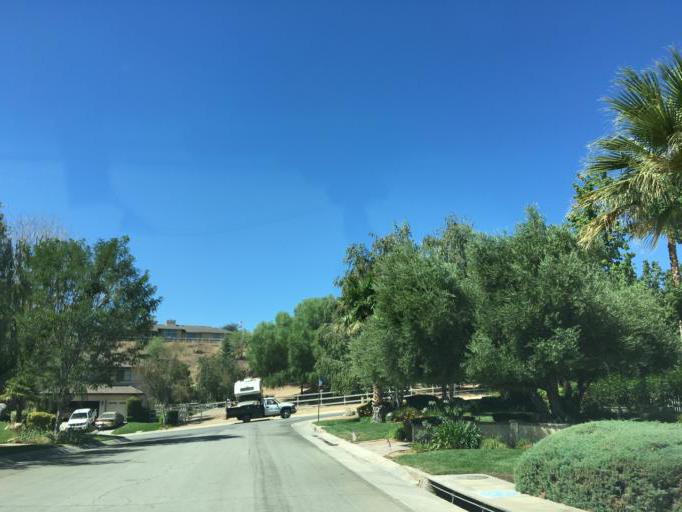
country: US
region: California
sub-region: Los Angeles County
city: Acton
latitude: 34.4751
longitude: -118.1734
